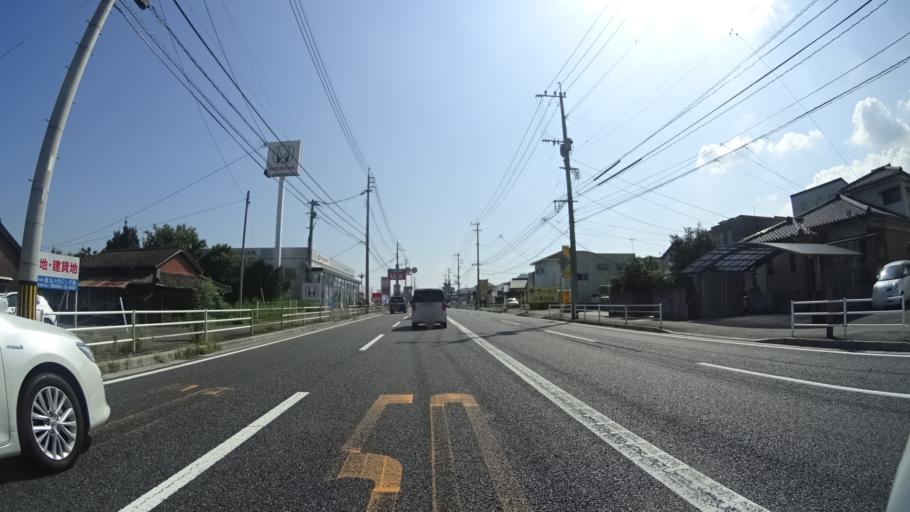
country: JP
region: Fukuoka
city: Kanda
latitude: 33.7723
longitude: 130.9813
